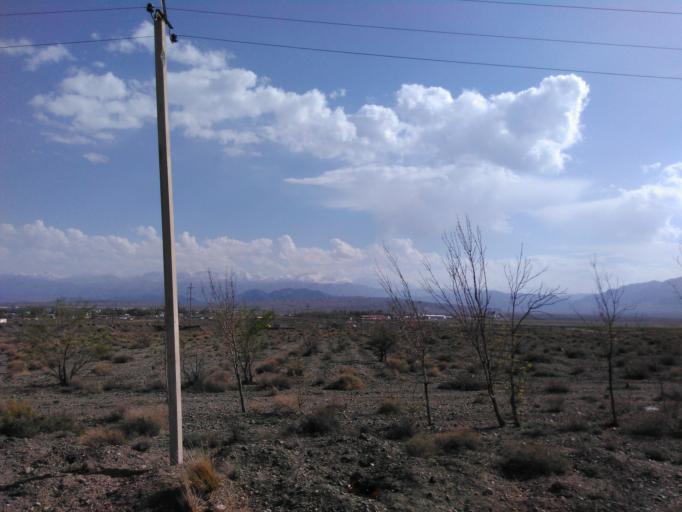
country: KG
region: Ysyk-Koel
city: Balykchy
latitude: 42.4555
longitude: 76.1510
